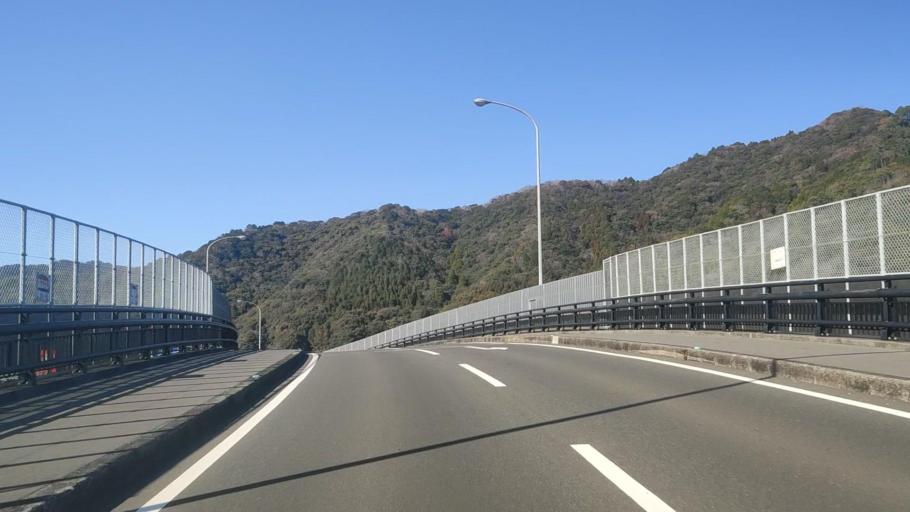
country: JP
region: Oita
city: Saiki
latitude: 32.9600
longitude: 131.8710
